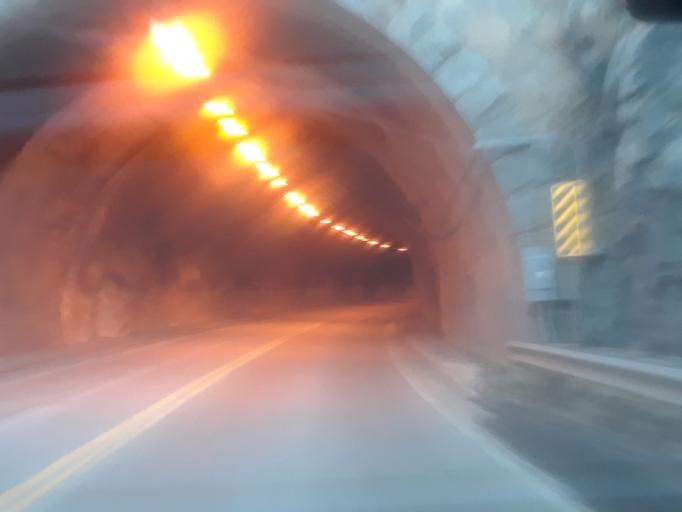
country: US
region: Colorado
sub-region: Clear Creek County
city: Idaho Springs
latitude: 39.7397
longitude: -105.4141
